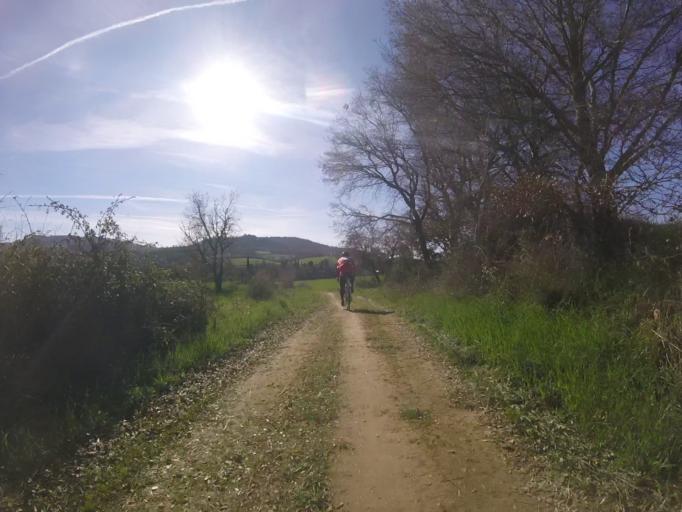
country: ES
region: Navarre
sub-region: Provincia de Navarra
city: Villatuerta
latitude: 42.6699
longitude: -1.9599
